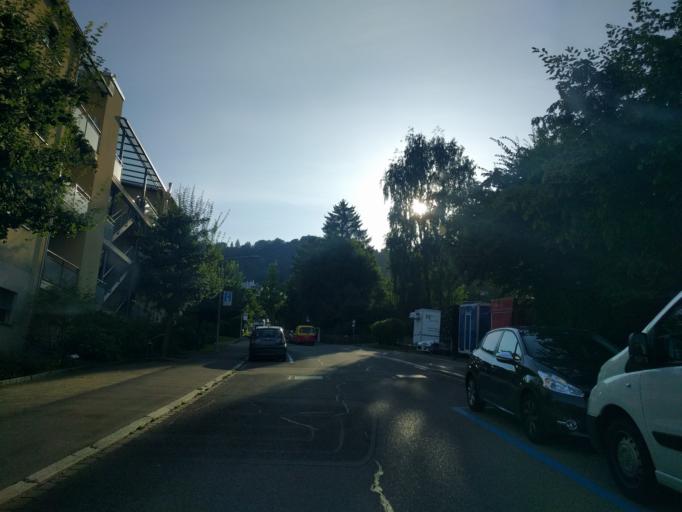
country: CH
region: Zurich
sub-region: Bezirk Zuerich
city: Zuerich (Kreis 2) / Mittel-Leimbach
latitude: 47.3251
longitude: 8.5128
